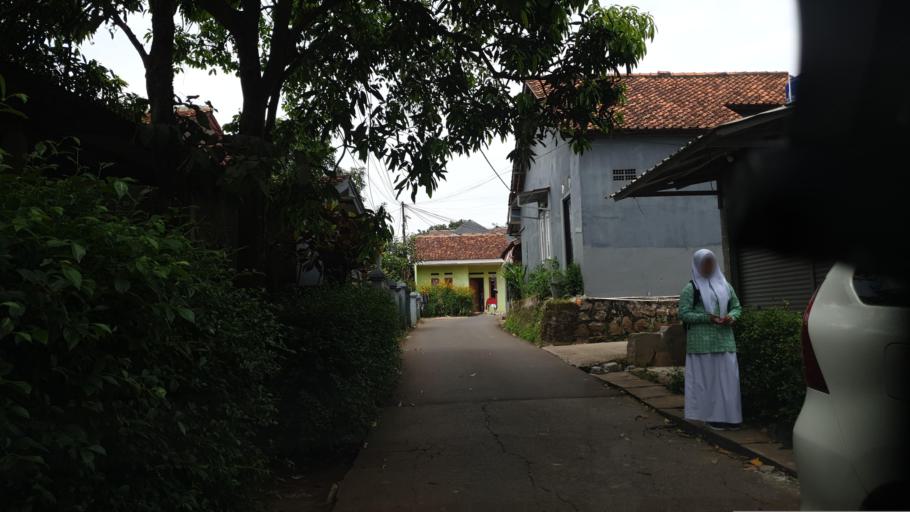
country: ID
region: West Java
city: Sawangan
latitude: -6.3778
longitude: 106.7645
